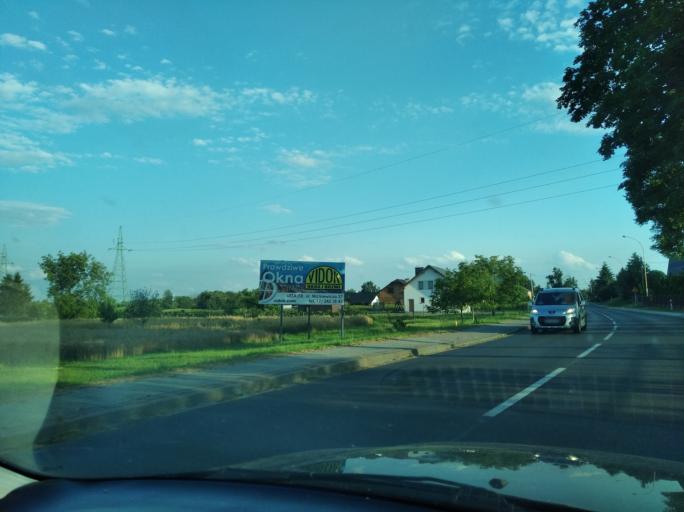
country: PL
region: Subcarpathian Voivodeship
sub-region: Powiat lezajski
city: Stare Miasto
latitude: 50.2780
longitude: 22.4278
